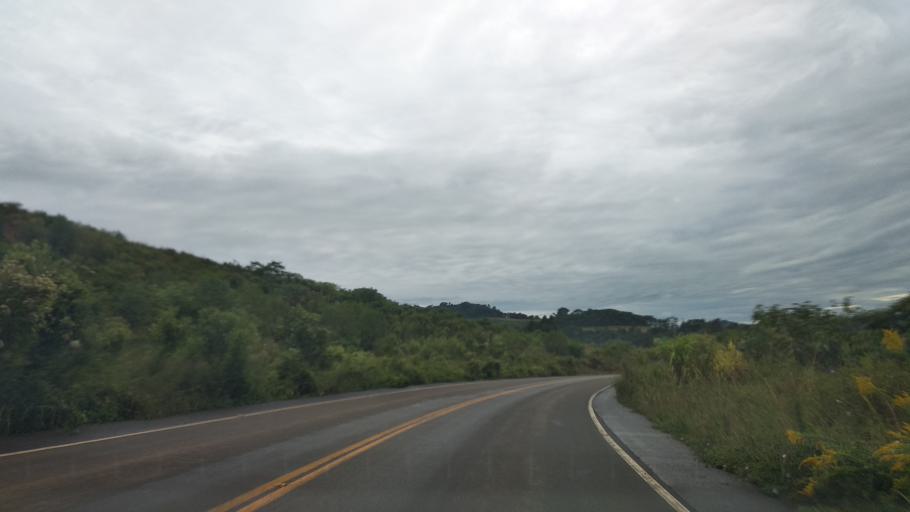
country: BR
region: Santa Catarina
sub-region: Videira
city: Videira
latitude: -27.0131
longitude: -51.1680
